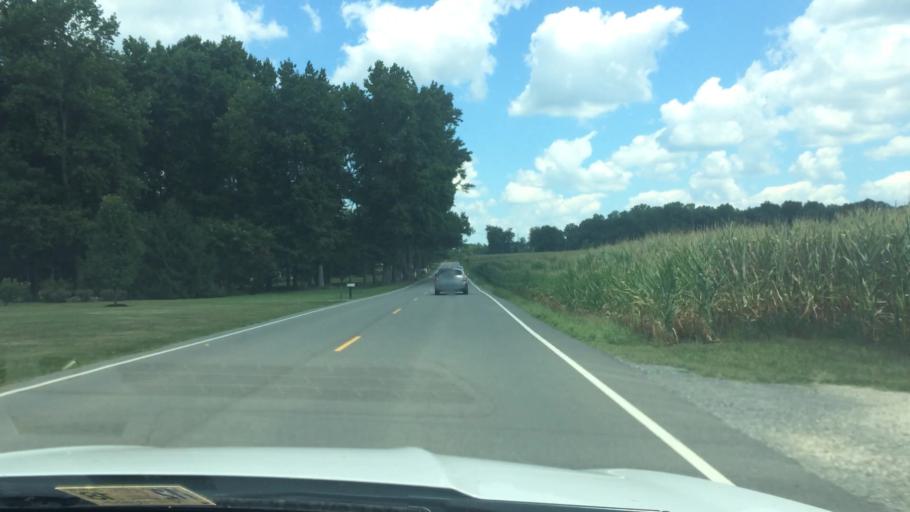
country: US
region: Virginia
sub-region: King William County
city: West Point
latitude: 37.5877
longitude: -76.7651
